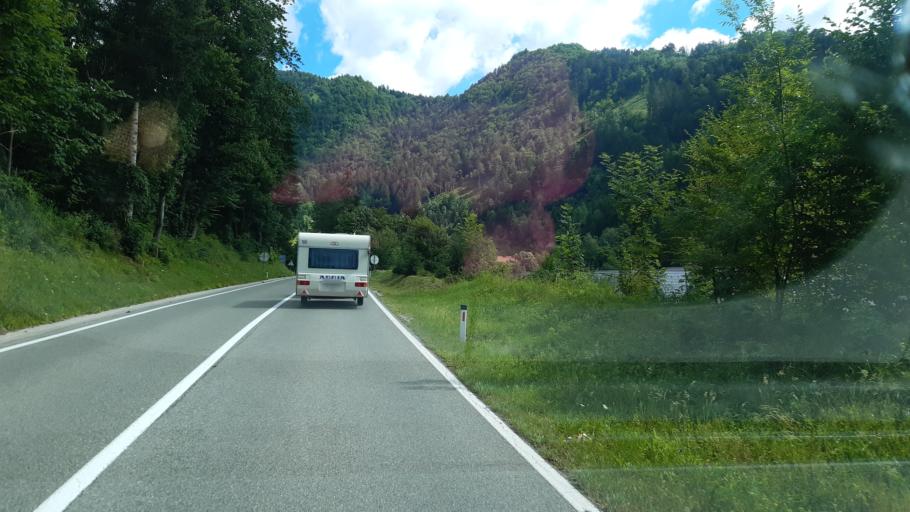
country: SI
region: Trzic
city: Trzic
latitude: 46.3658
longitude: 14.3061
